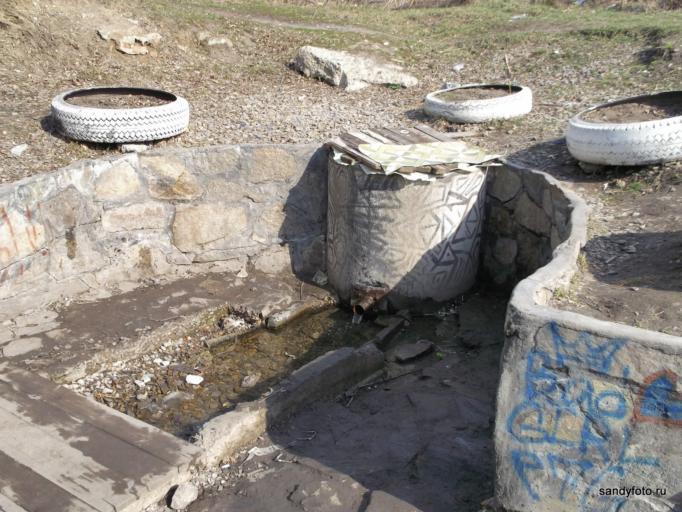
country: RU
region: Chelyabinsk
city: Troitsk
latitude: 54.0941
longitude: 61.5659
